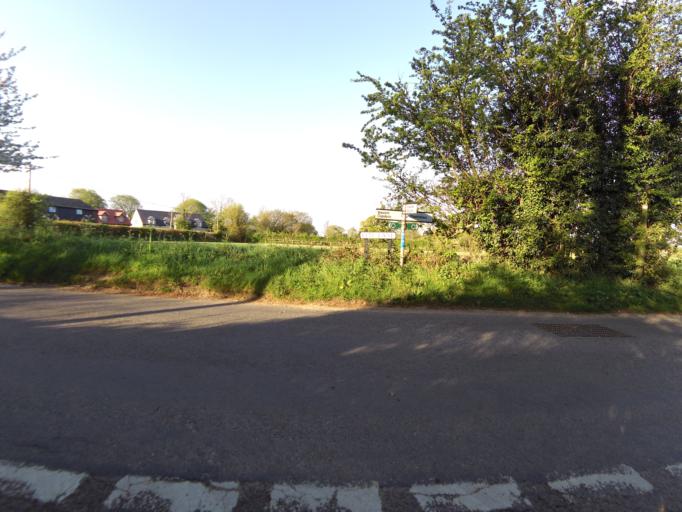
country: GB
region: England
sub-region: Suffolk
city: Capel Saint Mary
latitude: 52.0332
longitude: 1.0775
